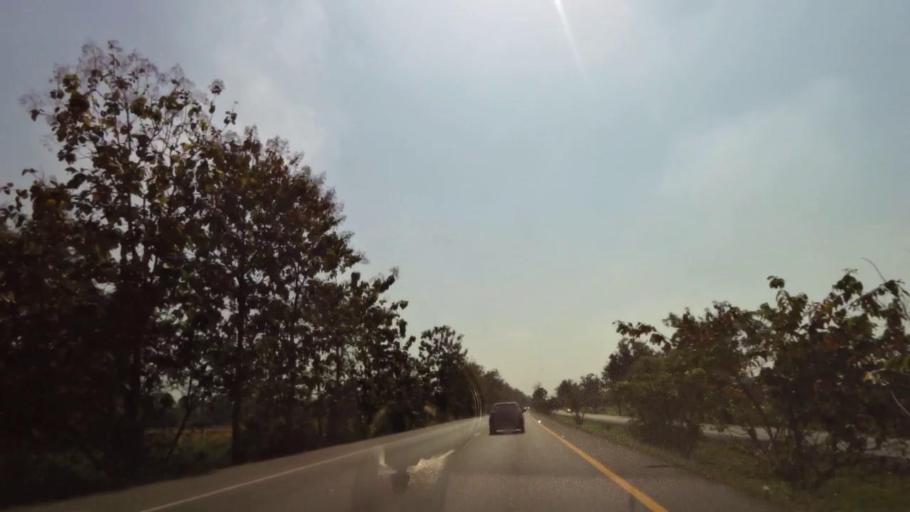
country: TH
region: Phichit
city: Bueng Na Rang
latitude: 16.0569
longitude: 100.1222
